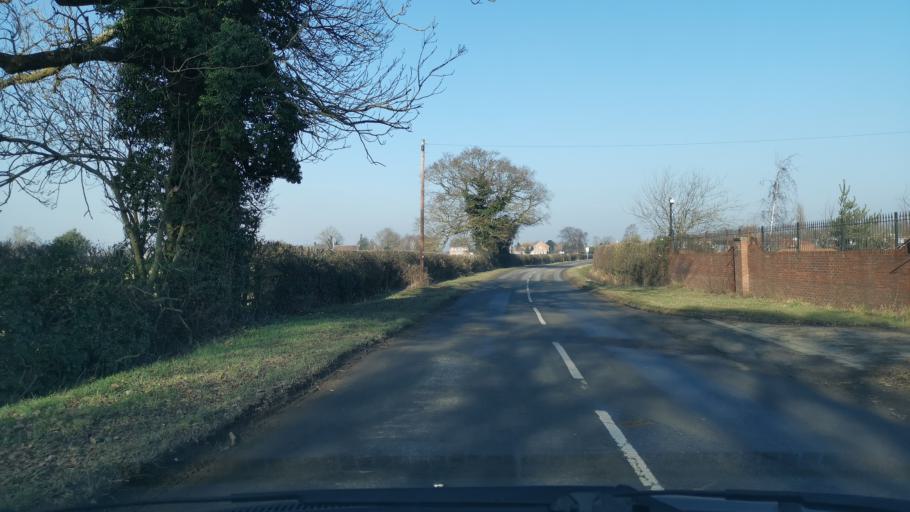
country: GB
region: England
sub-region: City of York
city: Murton
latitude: 53.9630
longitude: -1.0091
